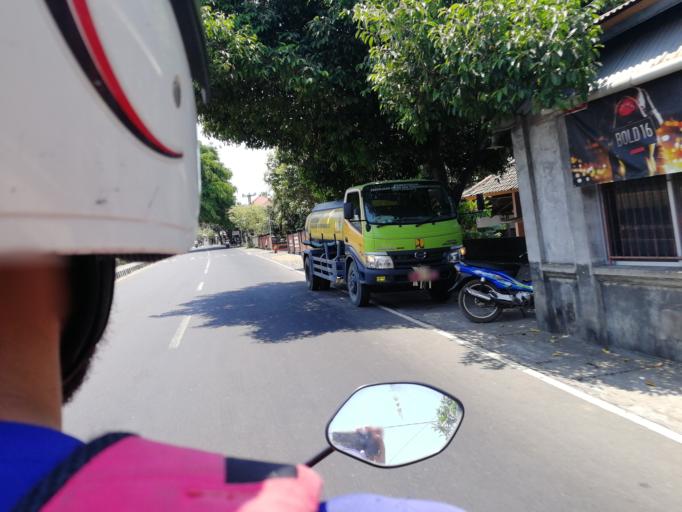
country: ID
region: Bali
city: Banjar Trunyan
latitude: -8.1450
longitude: 115.3987
